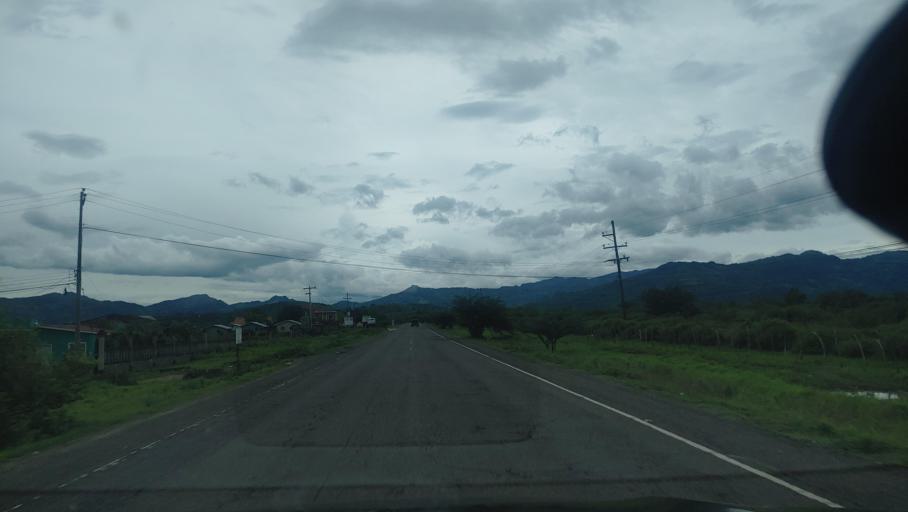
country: HN
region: Choluteca
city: Santa Ana de Yusguare
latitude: 13.3460
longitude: -87.1179
